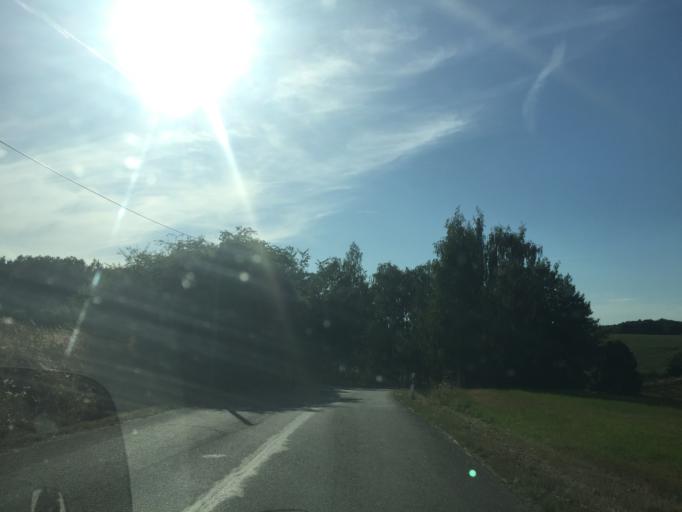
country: DE
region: Thuringia
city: Heyersdorf
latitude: 50.8598
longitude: 12.3331
